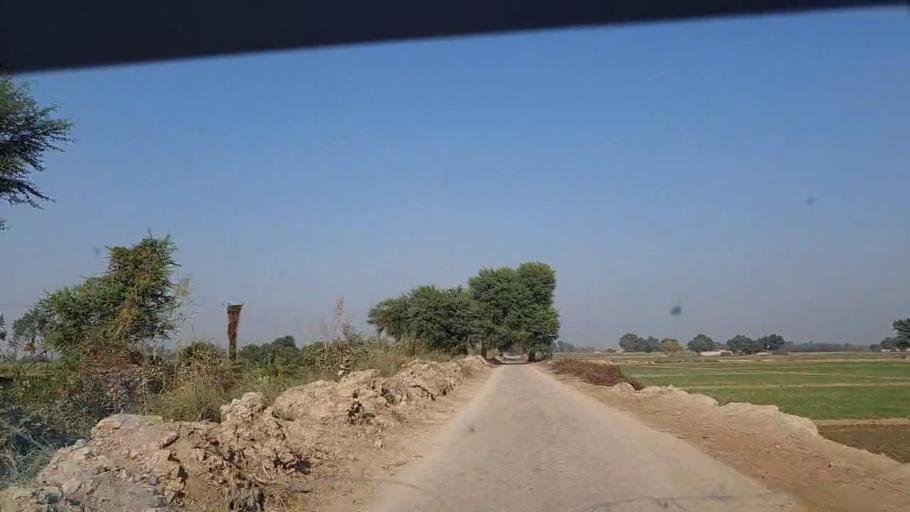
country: PK
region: Sindh
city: Hingorja
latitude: 27.2392
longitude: 68.3204
